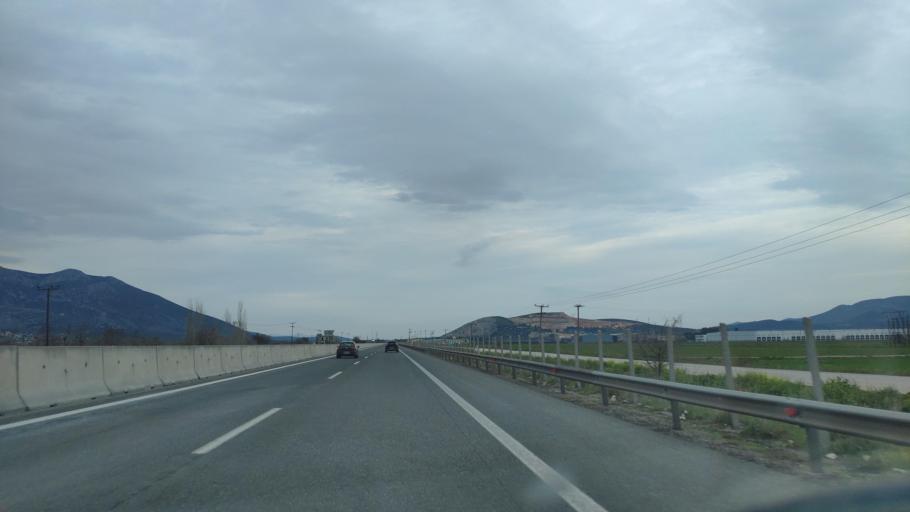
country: GR
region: Central Greece
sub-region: Nomos Voiotias
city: Thivai
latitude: 38.3676
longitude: 23.3547
